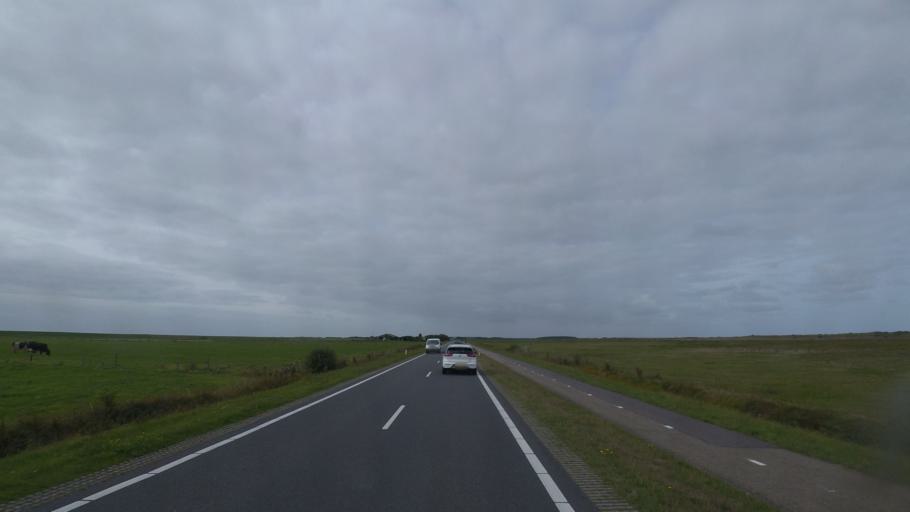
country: NL
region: Friesland
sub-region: Gemeente Ameland
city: Nes
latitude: 53.4457
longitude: 5.7516
